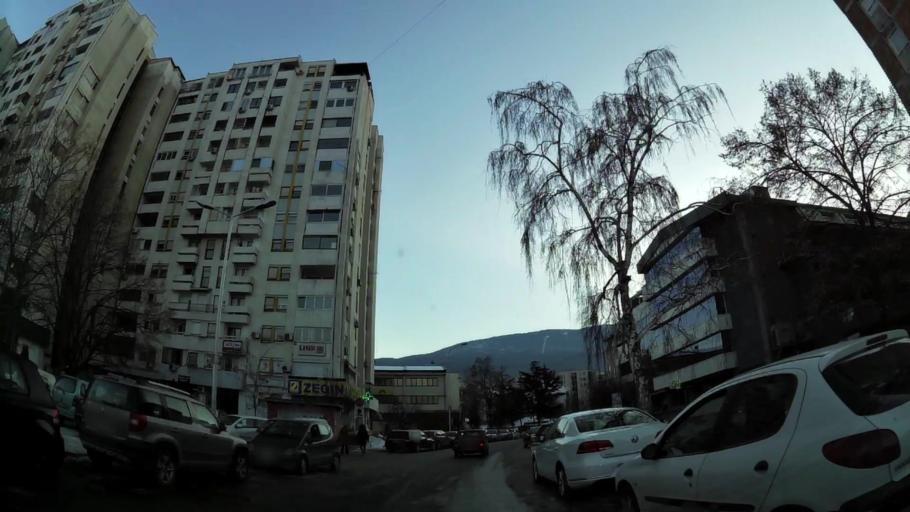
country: MK
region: Karpos
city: Skopje
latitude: 41.9930
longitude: 21.4204
